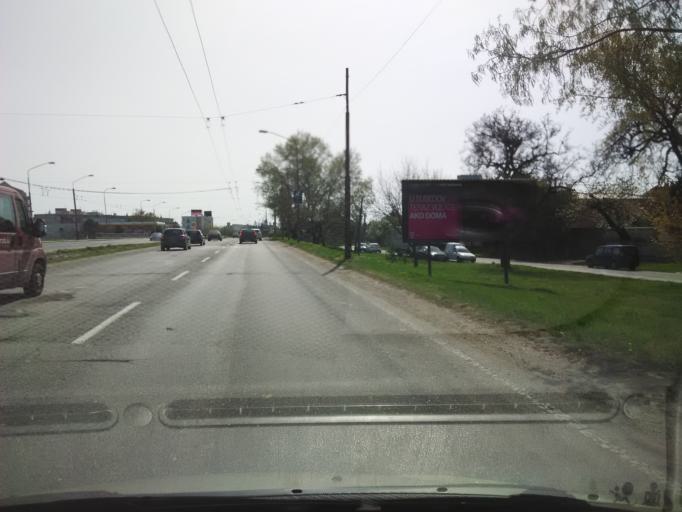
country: SK
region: Bratislavsky
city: Bratislava
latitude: 48.1418
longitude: 17.1913
